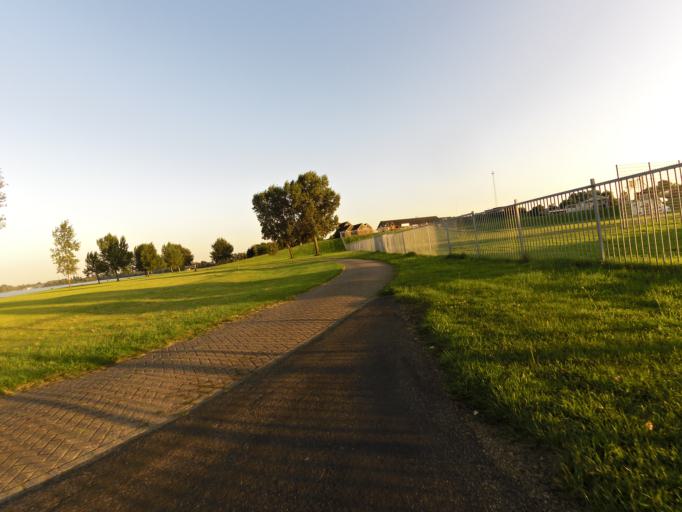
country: NL
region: Gelderland
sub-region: Gemeente Zevenaar
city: Zevenaar
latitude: 51.8688
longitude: 6.0770
